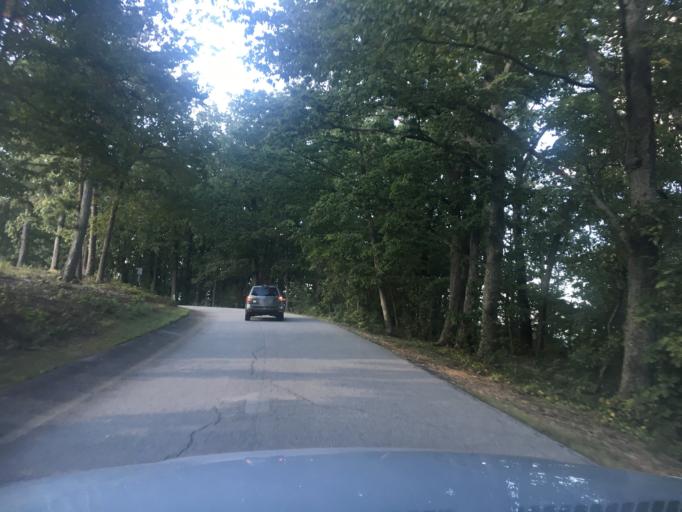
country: US
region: South Carolina
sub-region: Greenville County
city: Mauldin
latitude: 34.8399
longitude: -82.3069
